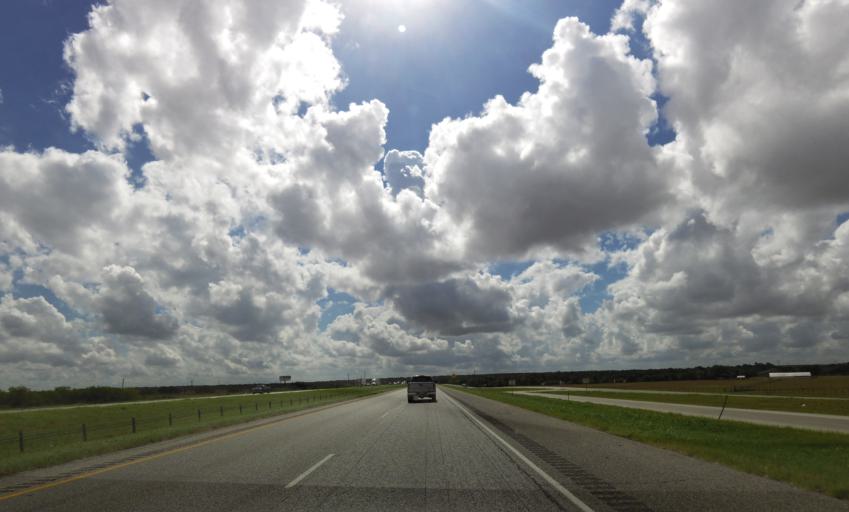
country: US
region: Texas
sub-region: Caldwell County
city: Luling
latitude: 29.6505
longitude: -97.5098
